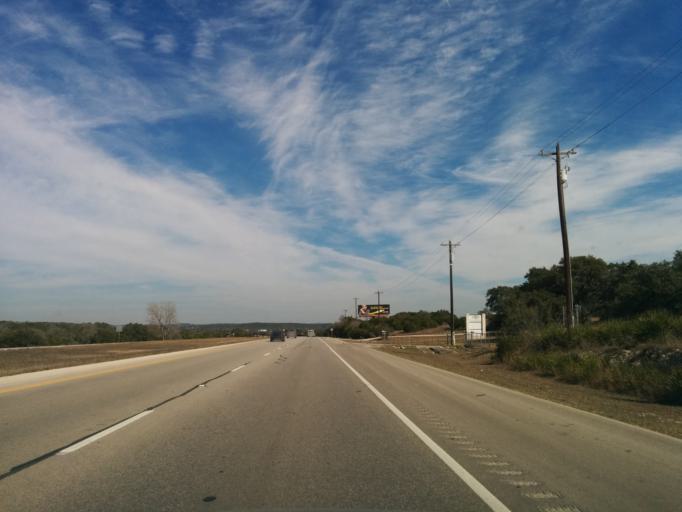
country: US
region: Texas
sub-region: Comal County
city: Bulverde
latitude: 29.8325
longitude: -98.4131
